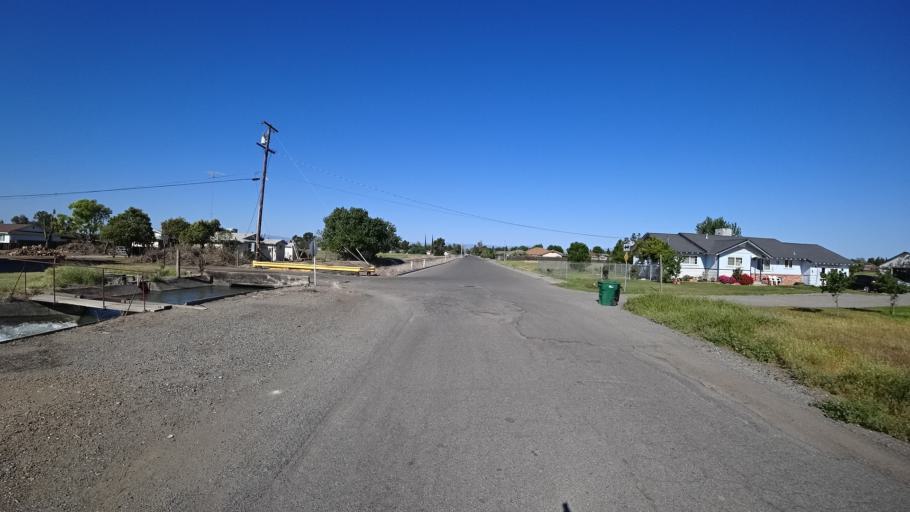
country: US
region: California
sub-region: Glenn County
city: Orland
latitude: 39.7509
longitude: -122.1731
